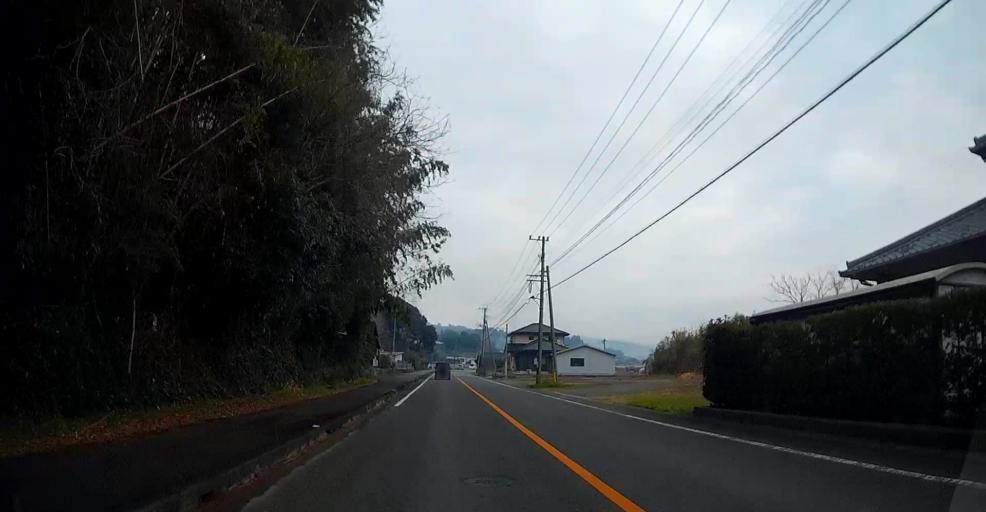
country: JP
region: Kumamoto
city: Yatsushiro
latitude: 32.6230
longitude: 130.5156
